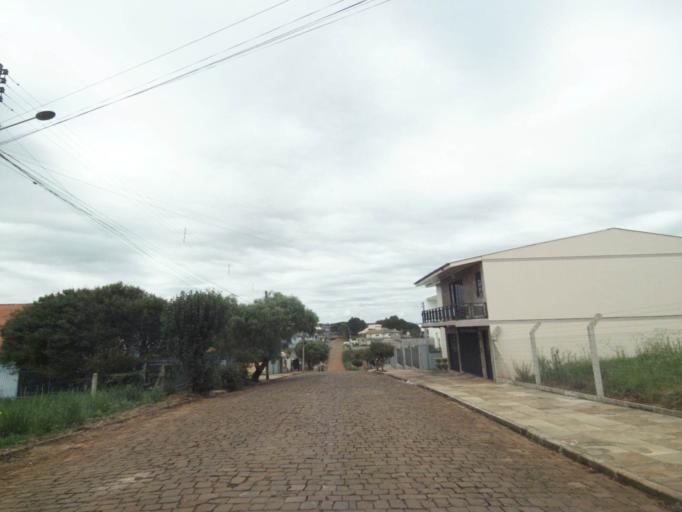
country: BR
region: Rio Grande do Sul
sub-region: Lagoa Vermelha
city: Lagoa Vermelha
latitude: -28.2145
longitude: -51.5309
